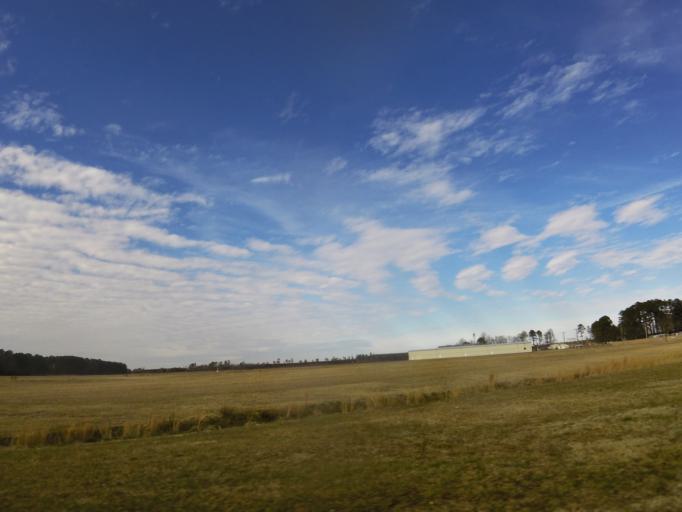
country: US
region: Virginia
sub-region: City of Franklin
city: Franklin
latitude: 36.6908
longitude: -76.8989
